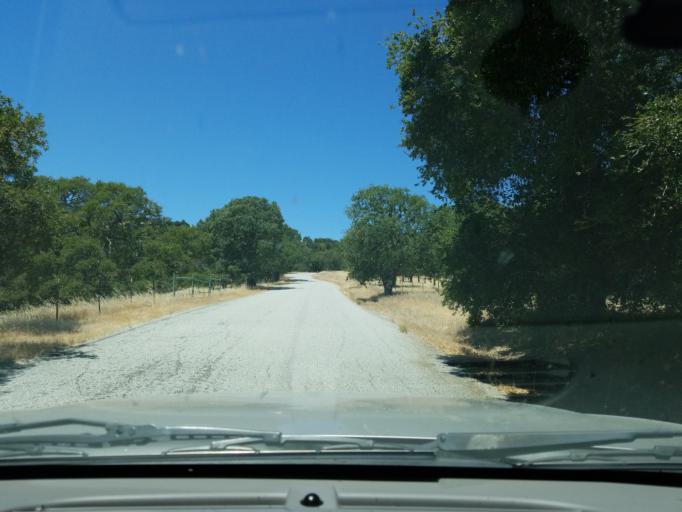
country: US
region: California
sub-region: Monterey County
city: Gonzales
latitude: 36.3411
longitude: -121.5206
